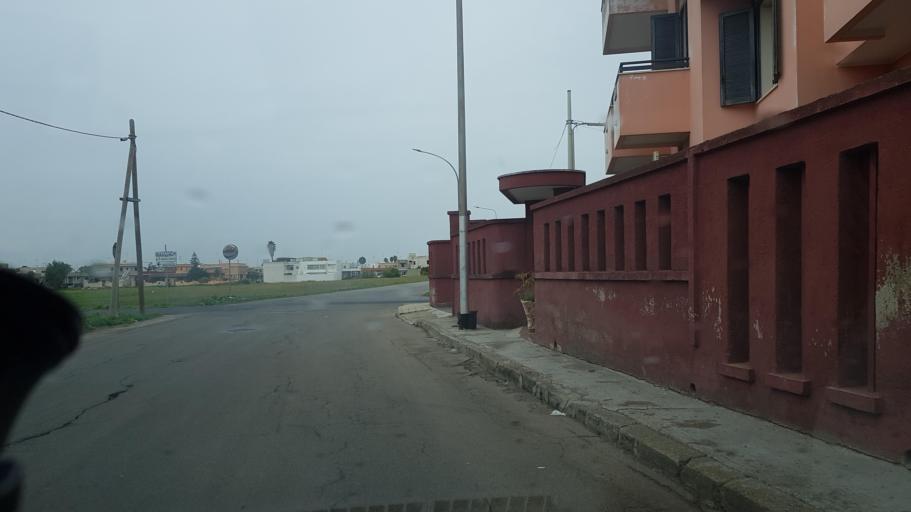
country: IT
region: Apulia
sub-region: Provincia di Lecce
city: Leverano
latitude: 40.2837
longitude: 17.9968
